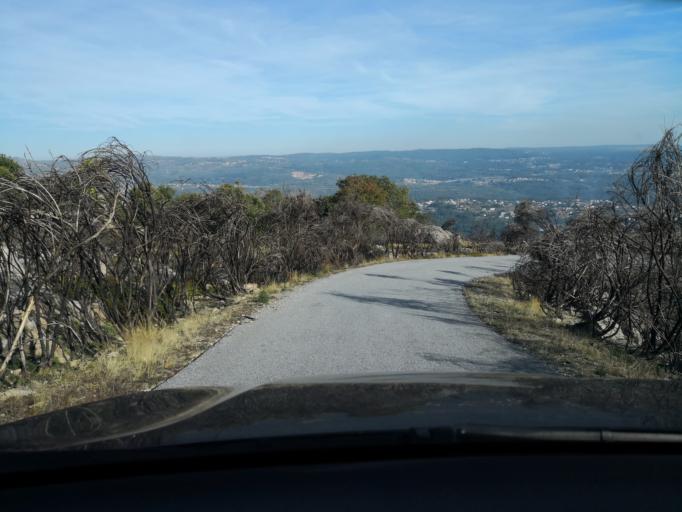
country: PT
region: Vila Real
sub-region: Vila Real
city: Vila Real
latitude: 41.3441
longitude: -7.7605
